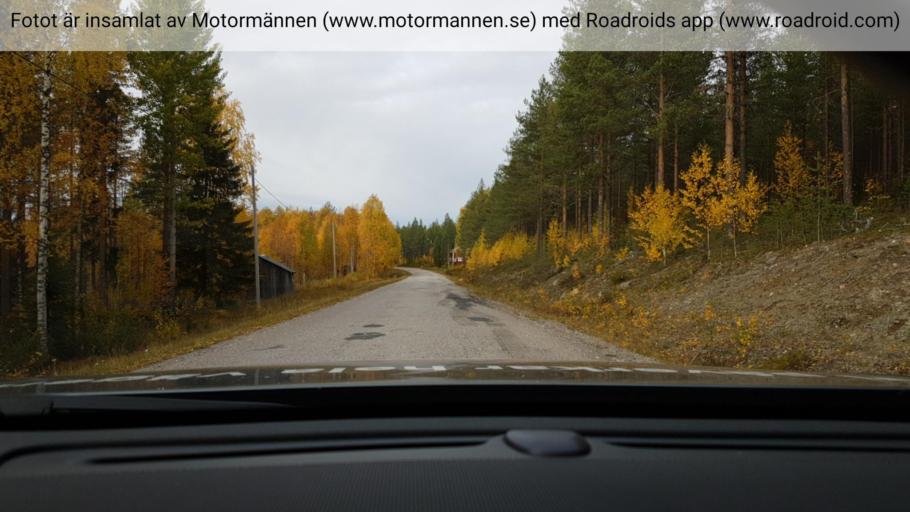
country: SE
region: Norrbotten
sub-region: Overkalix Kommun
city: OEverkalix
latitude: 66.2539
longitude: 23.1239
